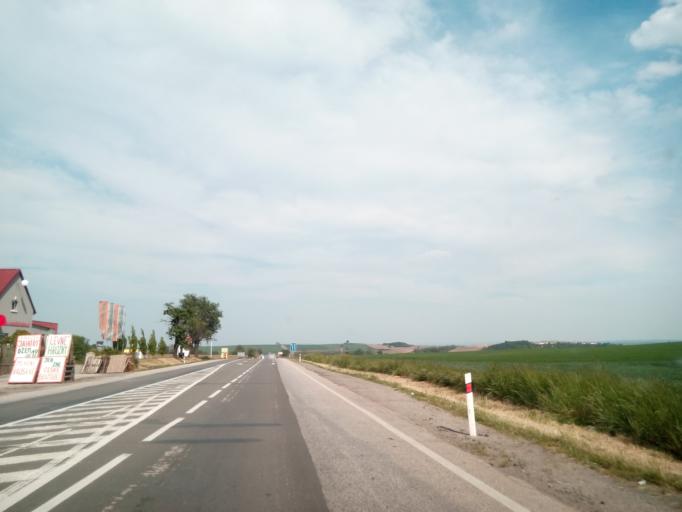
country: CZ
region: South Moravian
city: Podoli
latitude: 49.1823
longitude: 16.6990
